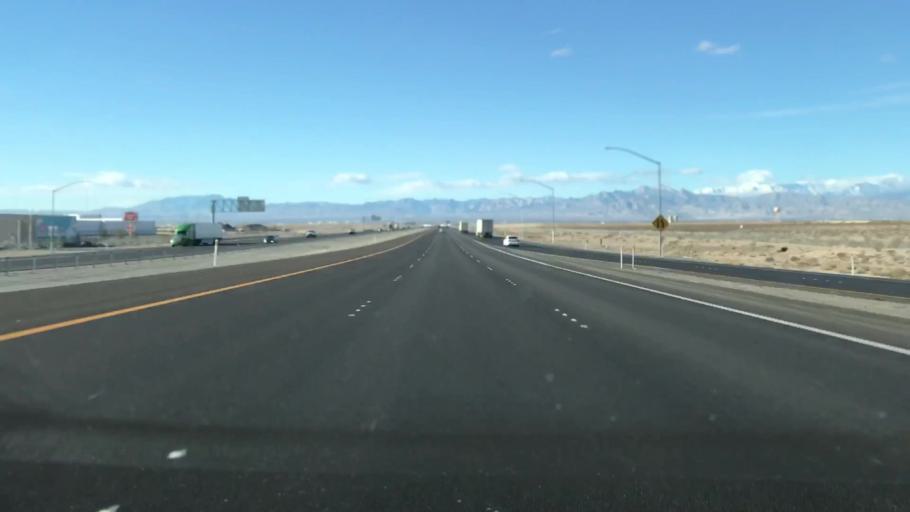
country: US
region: Nevada
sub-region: Clark County
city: Nellis Air Force Base
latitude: 36.2808
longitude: -115.0316
